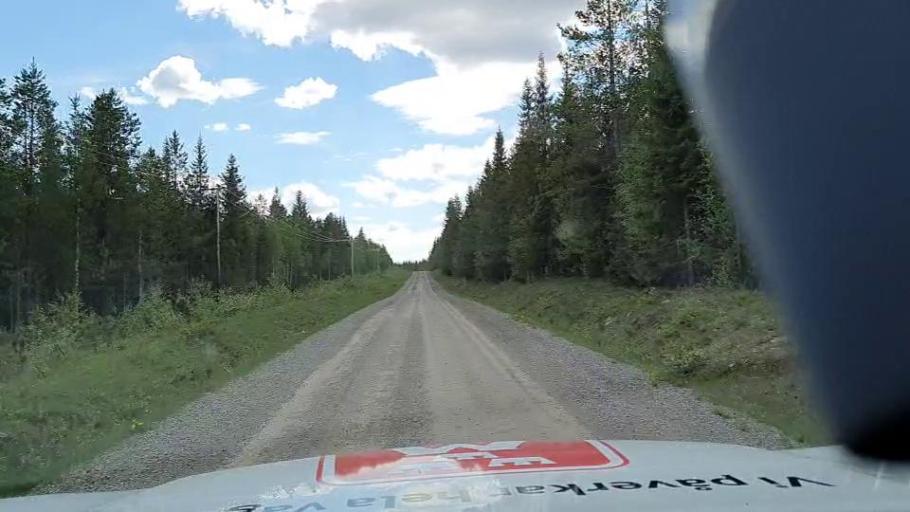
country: SE
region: Jaemtland
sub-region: Stroemsunds Kommun
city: Stroemsund
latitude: 64.5355
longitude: 15.5983
